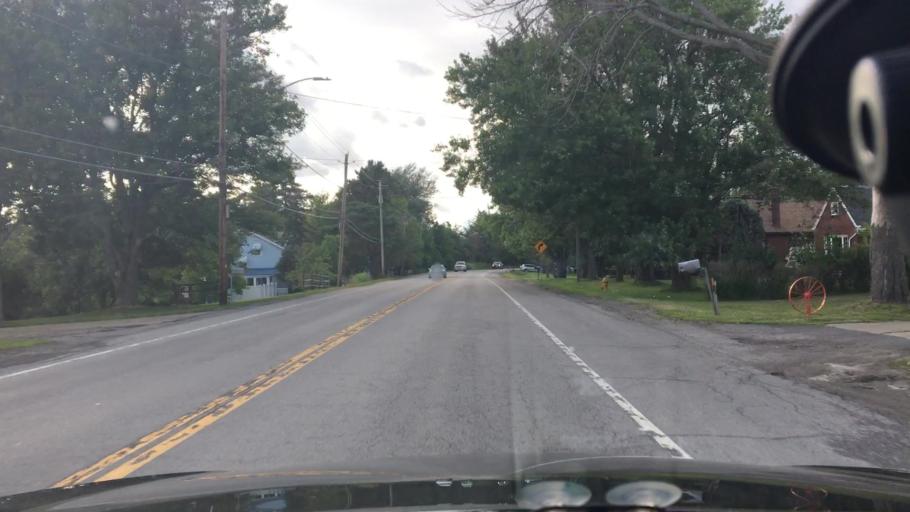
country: US
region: New York
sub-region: Erie County
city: Elma Center
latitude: 42.8313
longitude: -78.7062
